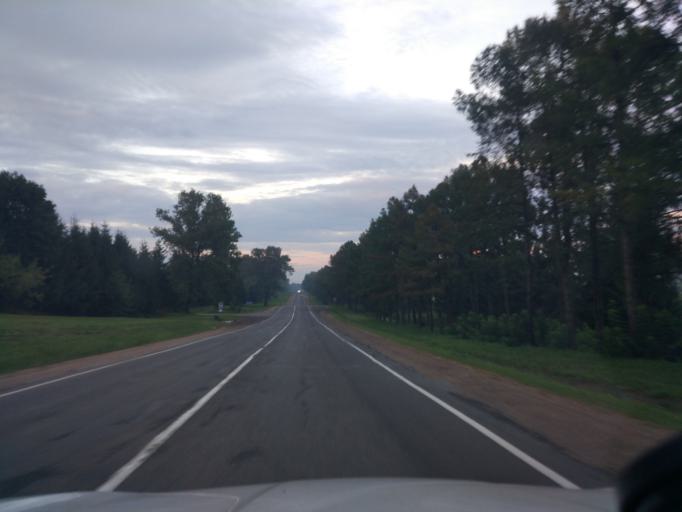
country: BY
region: Minsk
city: Astrashytski Haradok
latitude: 54.0783
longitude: 27.7087
